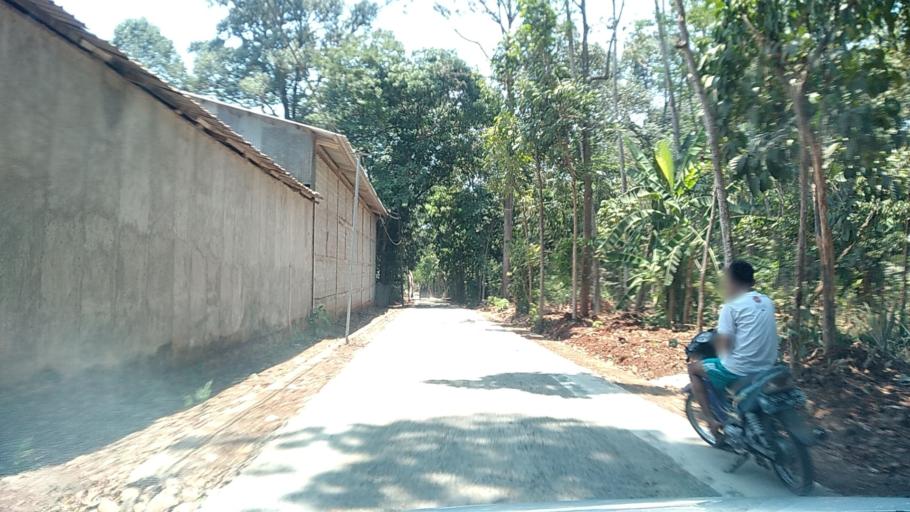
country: ID
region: Central Java
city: Ungaran
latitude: -7.0637
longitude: 110.3543
